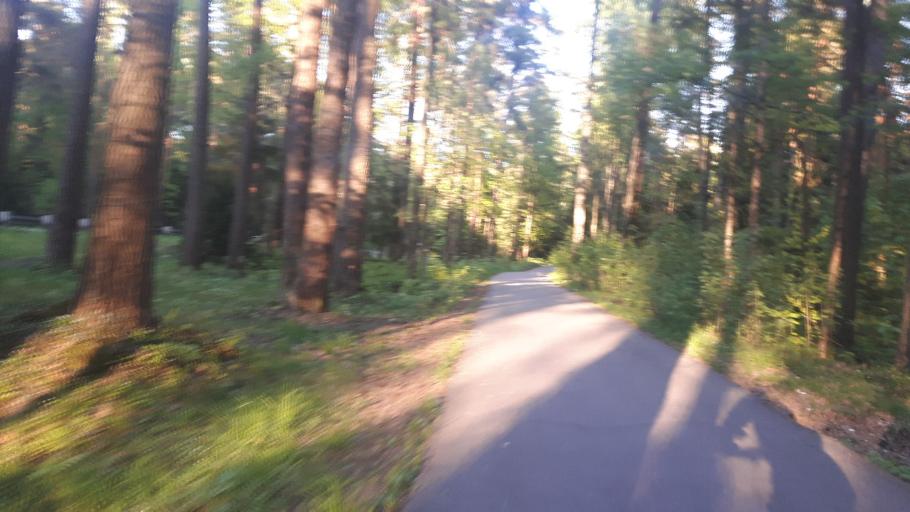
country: RU
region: Leningrad
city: Roshchino
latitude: 60.1933
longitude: 29.6293
